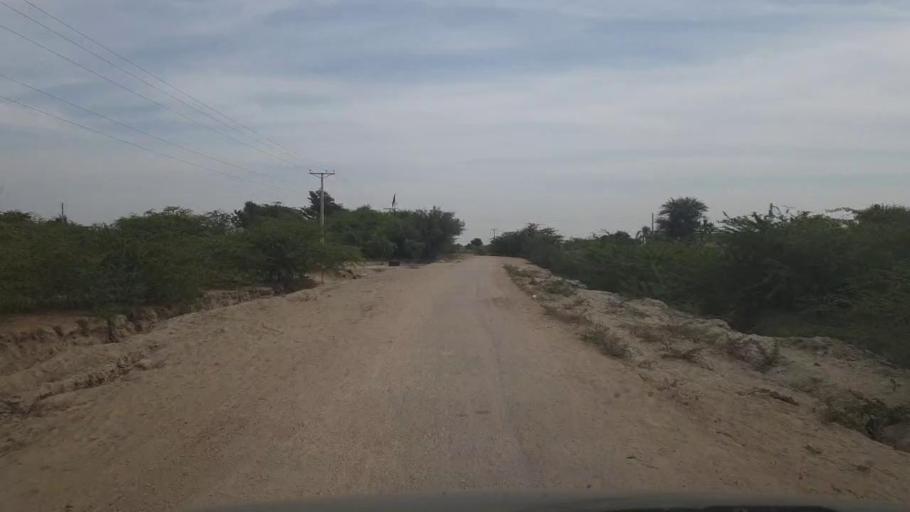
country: PK
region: Sindh
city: Kunri
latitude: 25.2530
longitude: 69.6287
